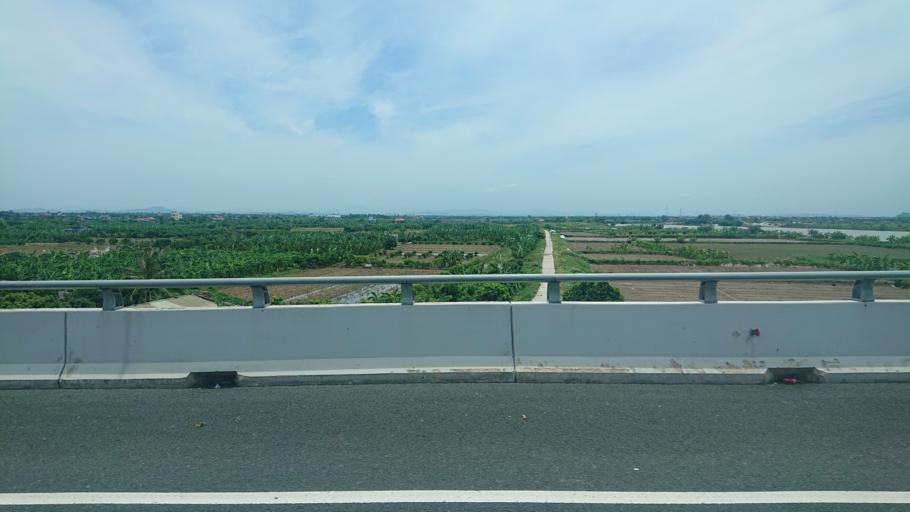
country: VN
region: Hai Phong
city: An Lao
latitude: 20.8089
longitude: 106.5102
